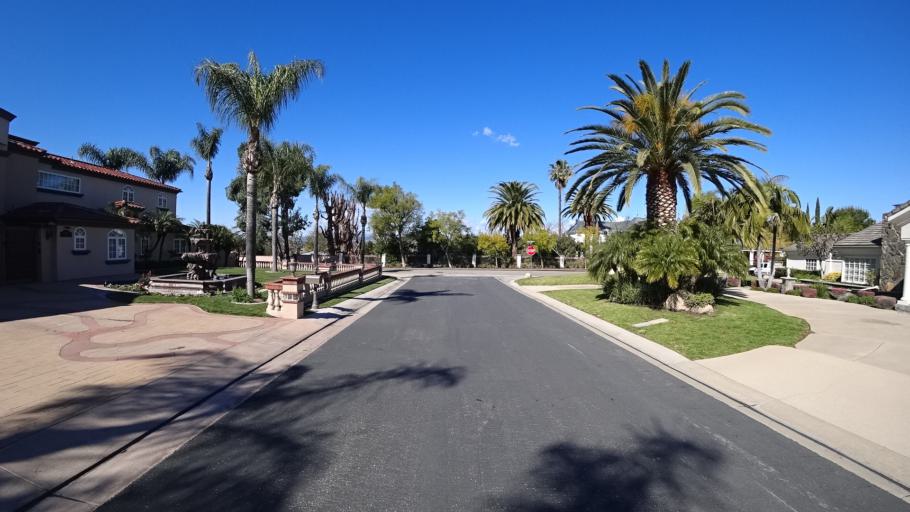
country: US
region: California
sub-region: Orange County
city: Villa Park
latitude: 33.8465
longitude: -117.8130
